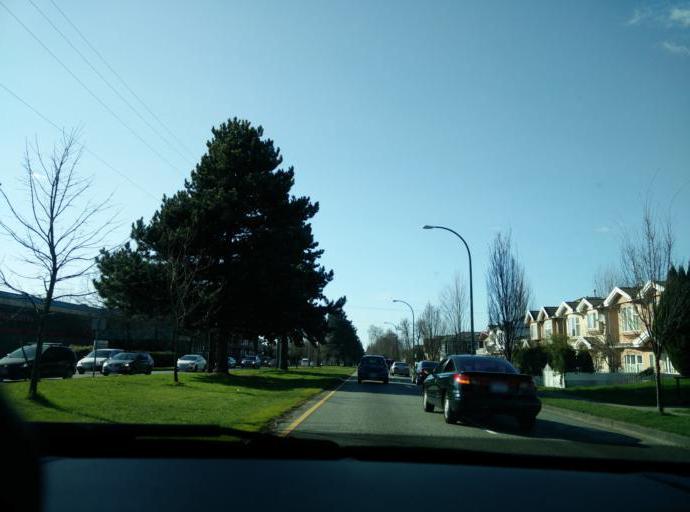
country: CA
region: British Columbia
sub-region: Fraser Valley Regional District
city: North Vancouver
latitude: 49.2696
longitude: -123.0455
